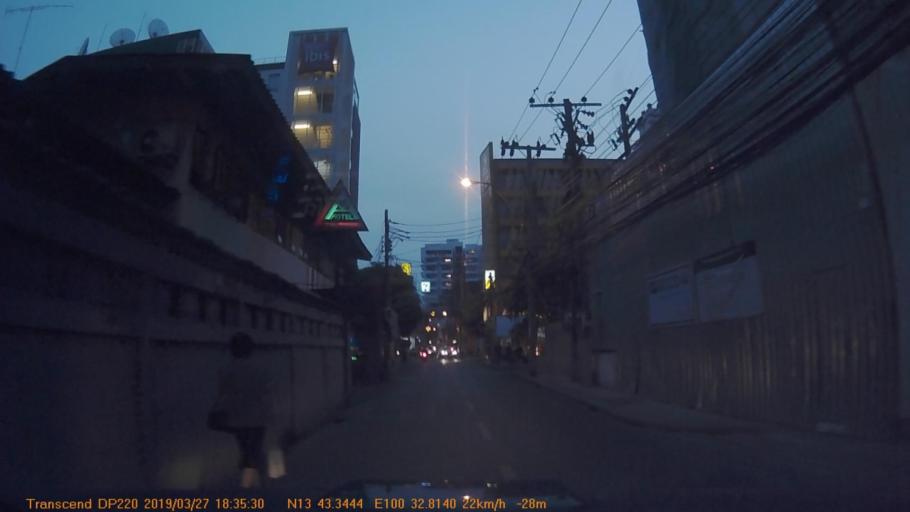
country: TH
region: Bangkok
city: Bang Rak
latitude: 13.7223
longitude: 100.5468
